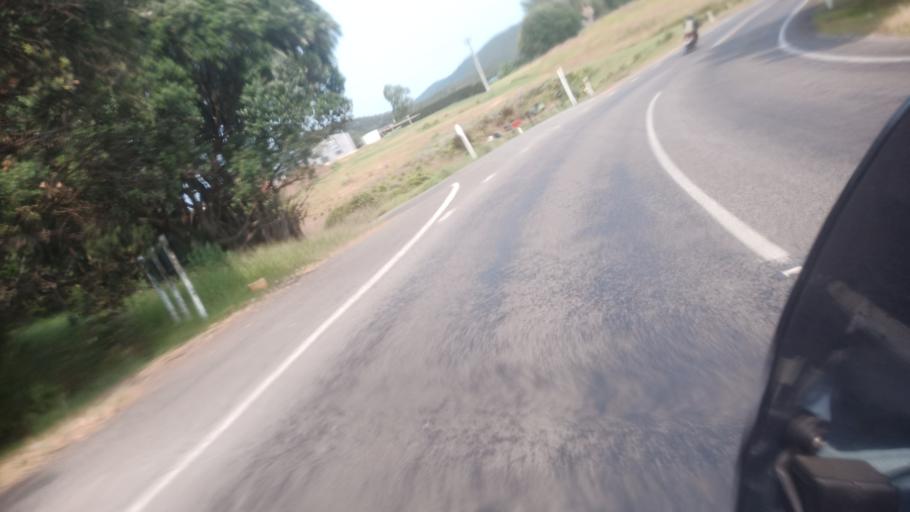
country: NZ
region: Bay of Plenty
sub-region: Opotiki District
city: Opotiki
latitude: -37.7529
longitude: 177.6836
